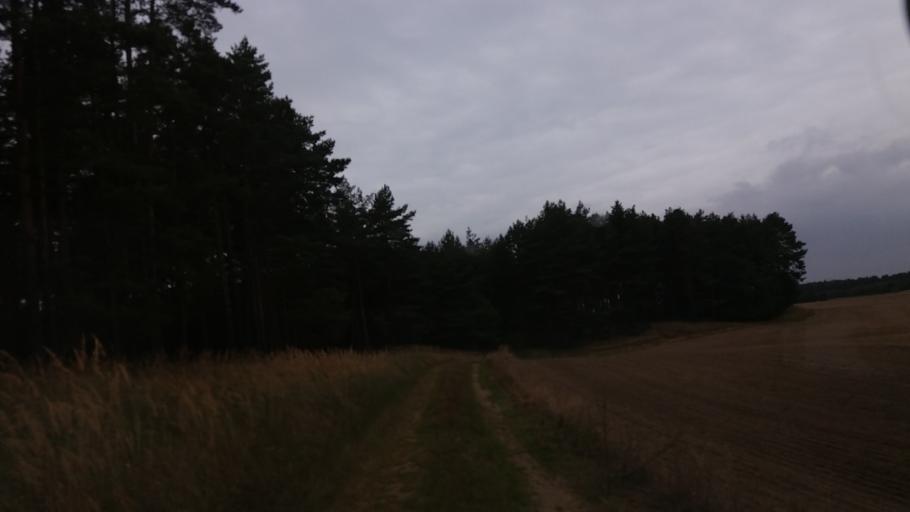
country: PL
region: West Pomeranian Voivodeship
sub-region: Powiat choszczenski
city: Bierzwnik
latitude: 52.9923
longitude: 15.5819
